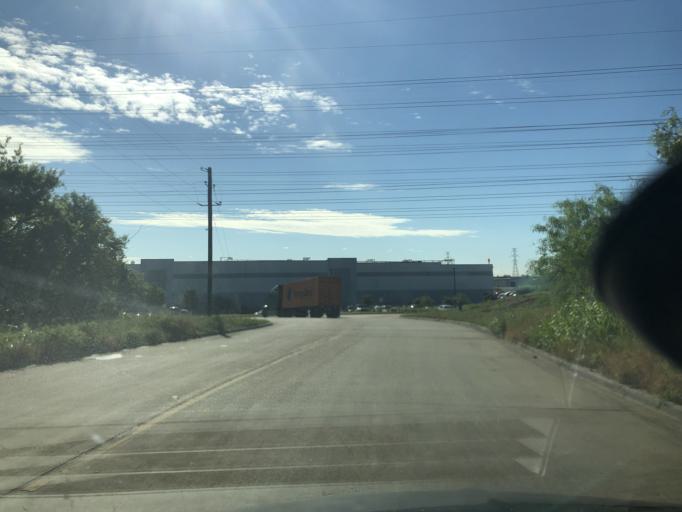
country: US
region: Texas
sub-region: Tarrant County
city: Euless
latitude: 32.8194
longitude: -97.0259
